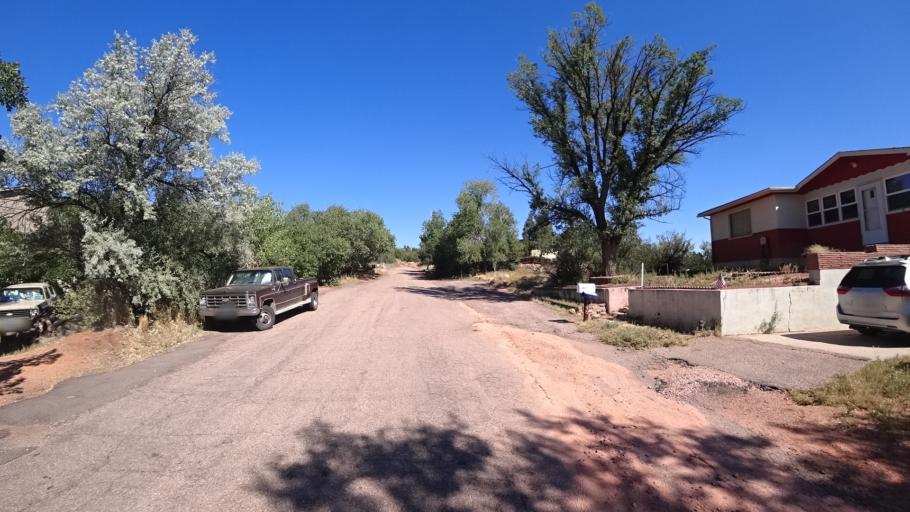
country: US
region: Colorado
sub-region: El Paso County
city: Manitou Springs
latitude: 38.8603
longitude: -104.8784
